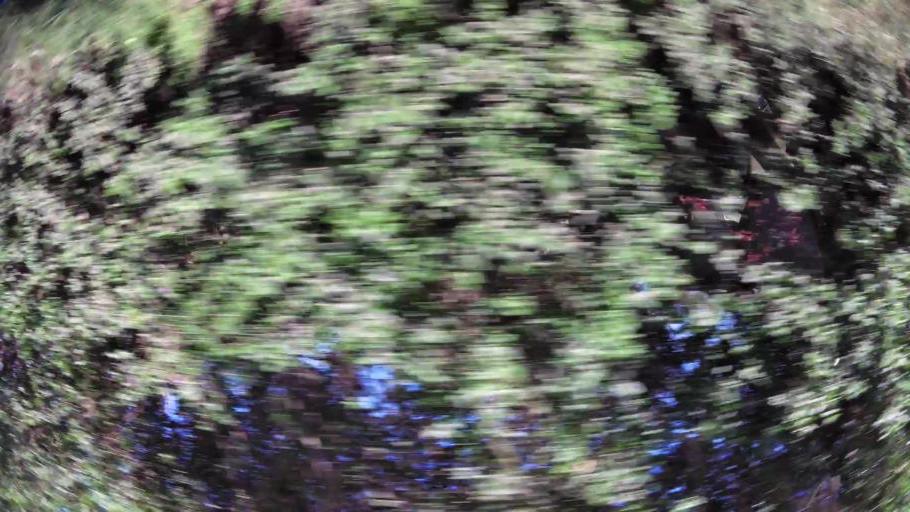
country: CL
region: Santiago Metropolitan
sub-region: Provincia de Talagante
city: Penaflor
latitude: -33.5949
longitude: -70.8802
